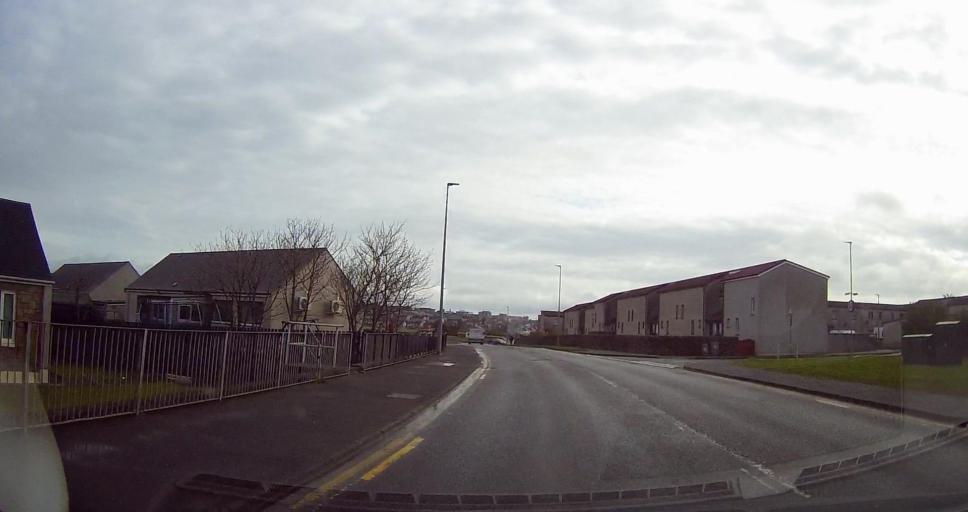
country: GB
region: Scotland
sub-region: Shetland Islands
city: Lerwick
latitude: 60.1463
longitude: -1.1686
